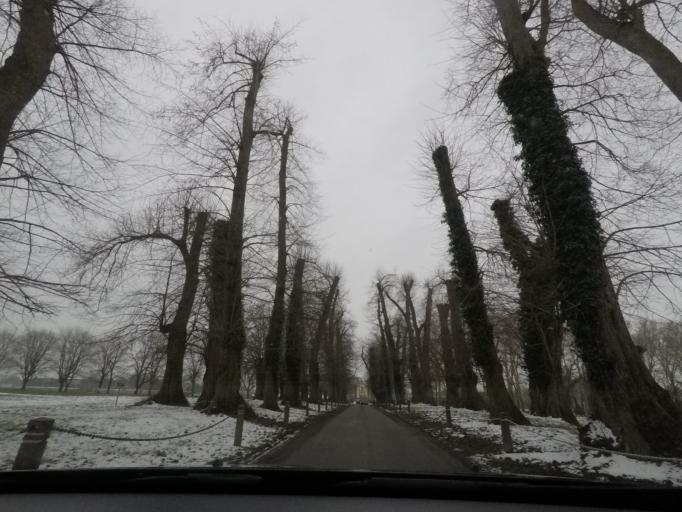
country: BE
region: Wallonia
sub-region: Province du Hainaut
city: Brugelette
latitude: 50.5901
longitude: 3.8873
